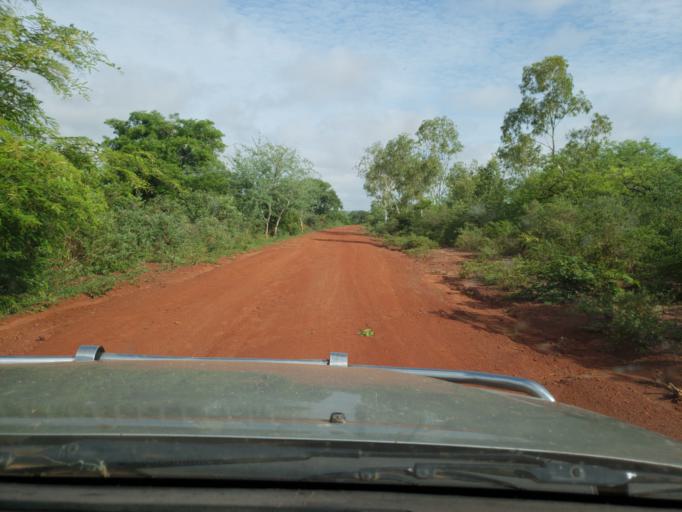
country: ML
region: Sikasso
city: Koutiala
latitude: 12.3903
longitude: -5.9750
